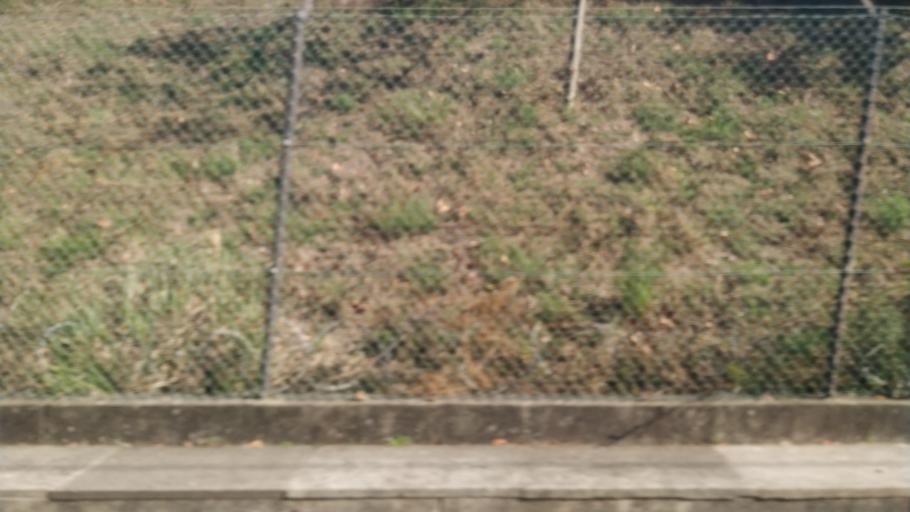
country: PT
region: Porto
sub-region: Matosinhos
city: Senhora da Hora
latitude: 41.1838
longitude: -8.6643
